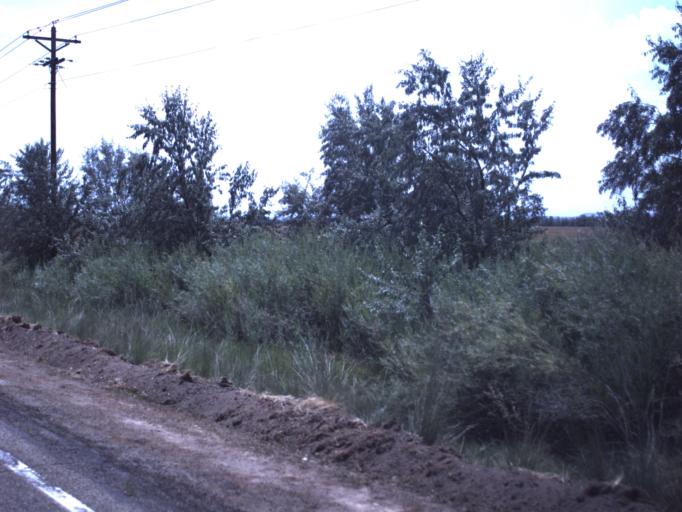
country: US
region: Utah
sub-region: Duchesne County
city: Roosevelt
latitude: 40.3858
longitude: -110.0298
